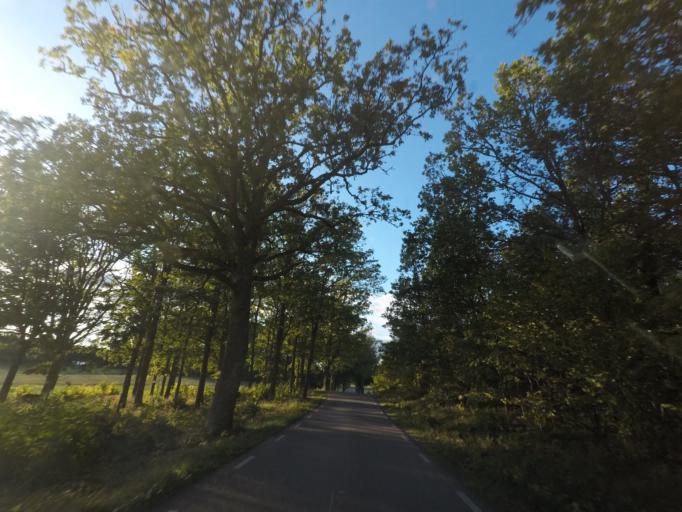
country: SE
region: Vaestmanland
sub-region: Kungsors Kommun
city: Kungsoer
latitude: 59.4857
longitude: 16.1776
